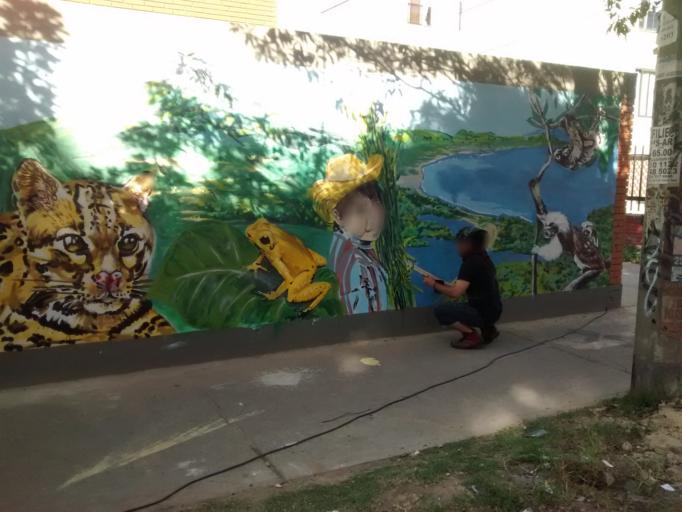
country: CO
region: Bogota D.C.
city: Bogota
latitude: 4.6690
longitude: -74.1332
